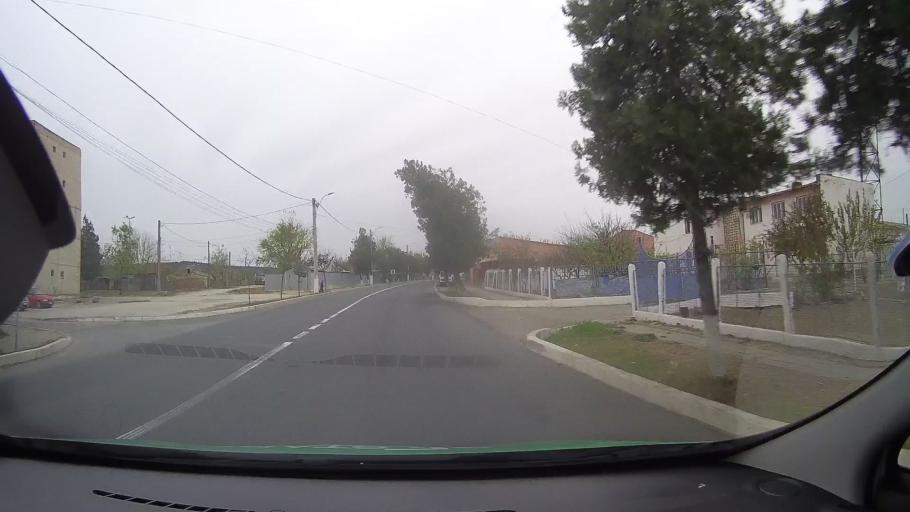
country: RO
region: Constanta
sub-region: Oras Harsova
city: Harsova
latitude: 44.6900
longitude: 27.9424
